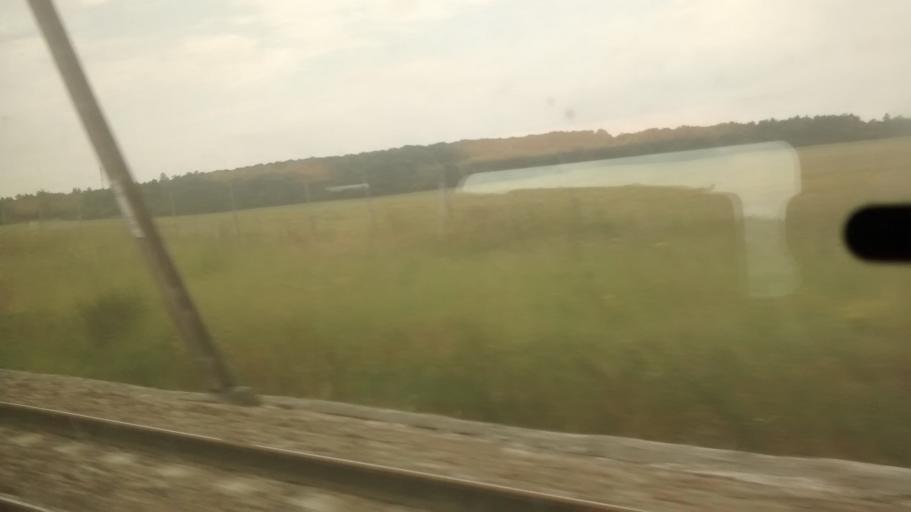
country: FR
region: Bourgogne
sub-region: Departement de l'Yonne
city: Ravieres
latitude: 47.5902
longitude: 4.1325
